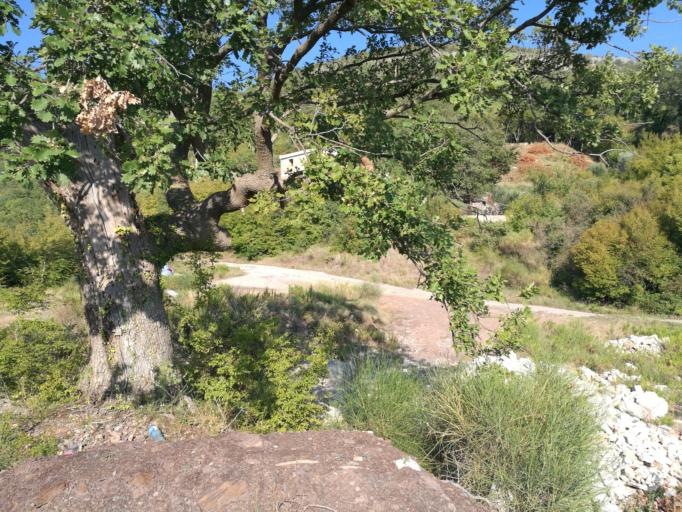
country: ME
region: Budva
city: Budva
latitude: 42.2822
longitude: 18.8891
